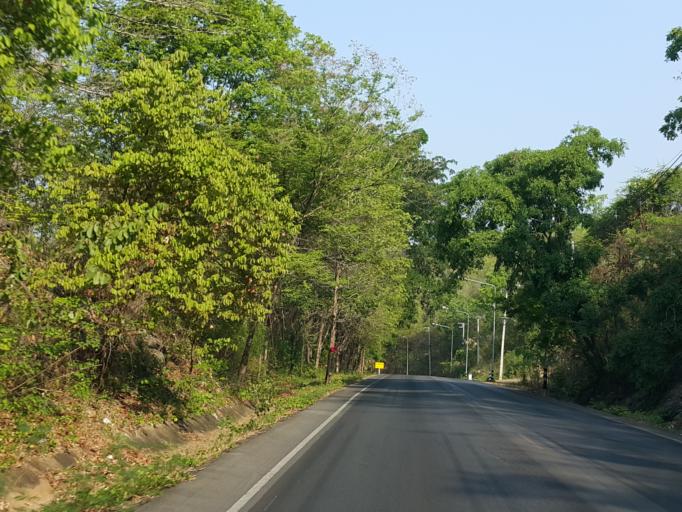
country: TH
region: Kanchanaburi
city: Sai Yok
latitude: 14.1169
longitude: 99.1515
